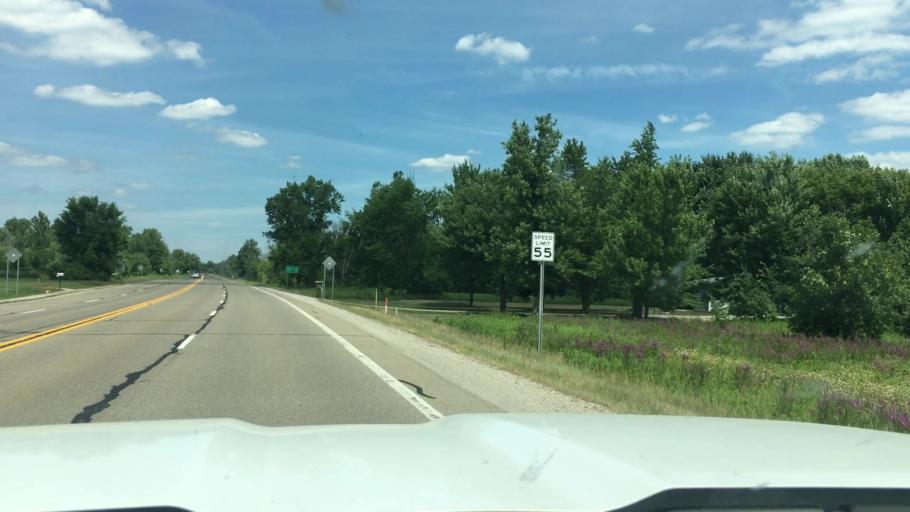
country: US
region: Michigan
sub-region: Lapeer County
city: Barnes Lake-Millers Lake
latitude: 43.2205
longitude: -83.3135
